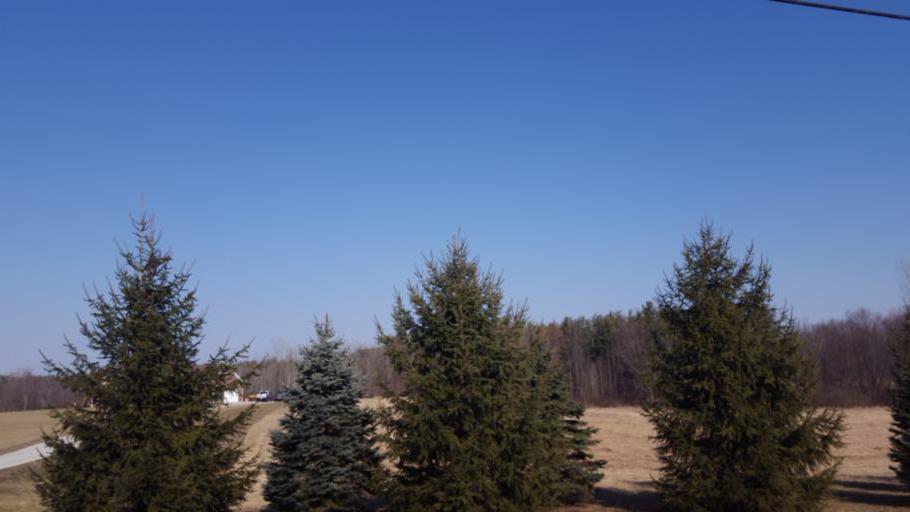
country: US
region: Ohio
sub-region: Richland County
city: Shelby
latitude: 40.8431
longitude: -82.6087
